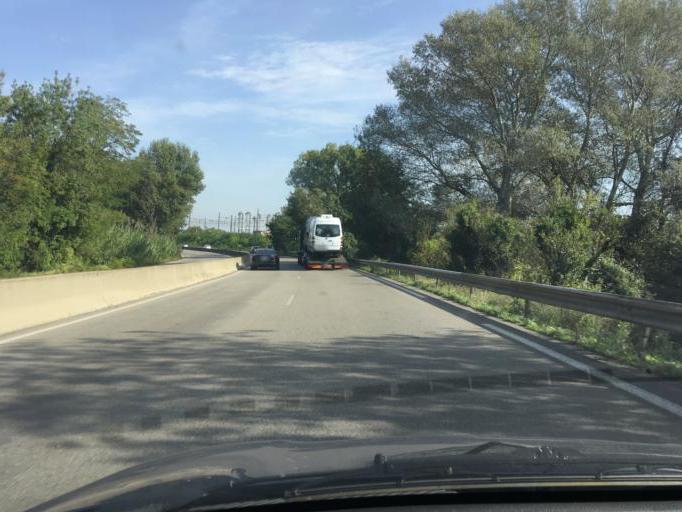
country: FR
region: Languedoc-Roussillon
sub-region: Departement du Gard
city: Les Angles
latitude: 43.9479
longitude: 4.7760
